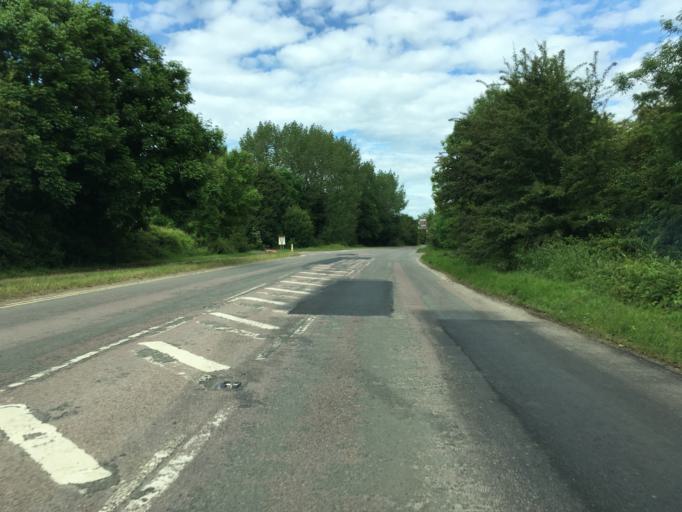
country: GB
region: England
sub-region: Wiltshire
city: Minety
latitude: 51.6535
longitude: -1.9642
